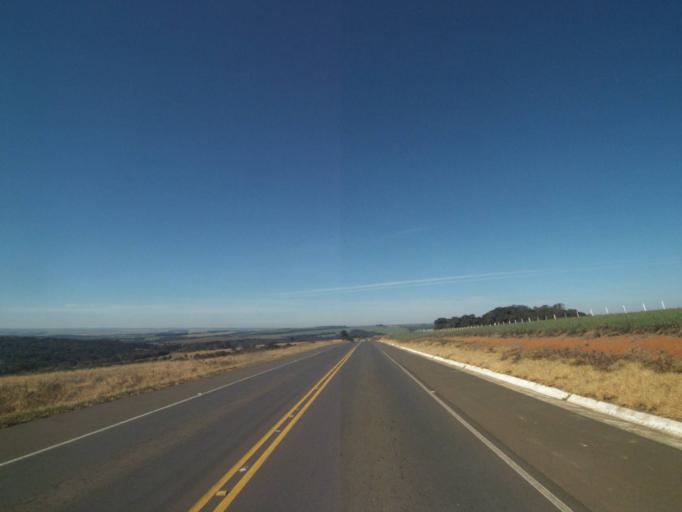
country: BR
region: Parana
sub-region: Tibagi
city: Tibagi
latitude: -24.6384
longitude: -50.4593
